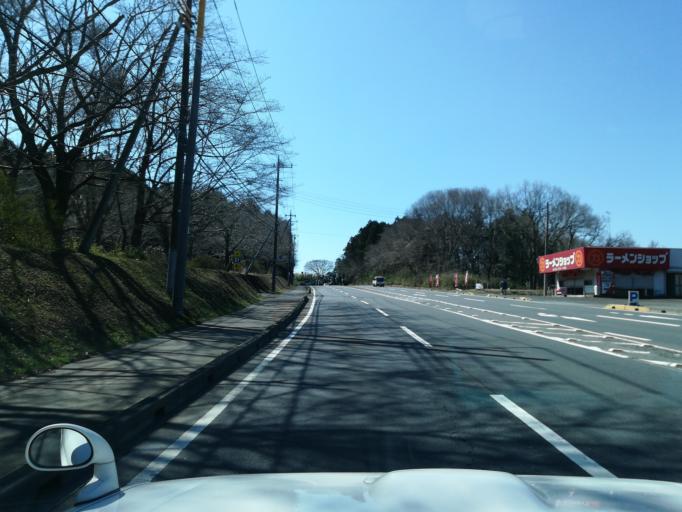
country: JP
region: Ibaraki
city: Ushiku
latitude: 35.9666
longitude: 140.1713
